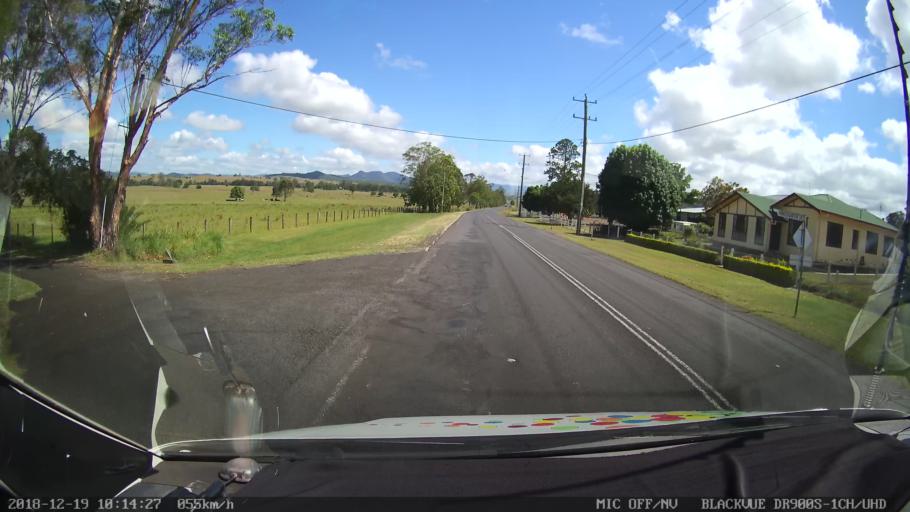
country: AU
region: New South Wales
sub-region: Kyogle
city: Kyogle
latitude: -28.6142
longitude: 153.0093
